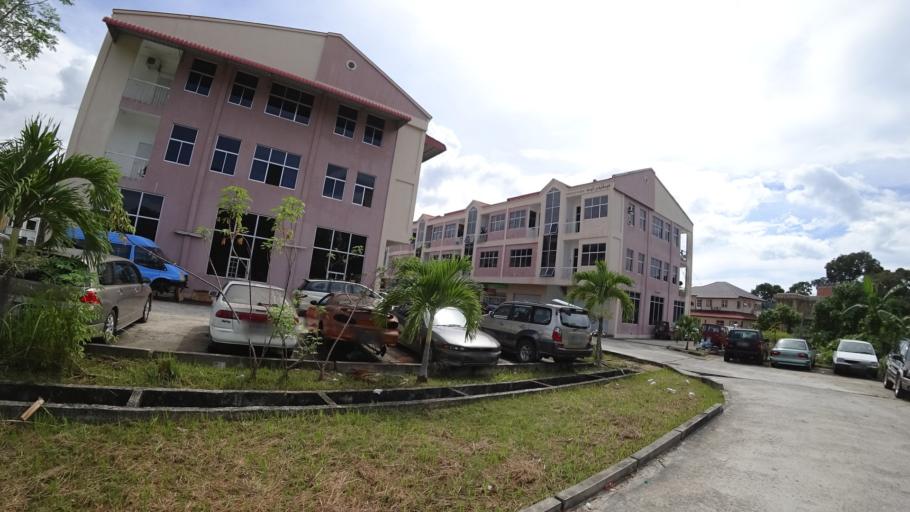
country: BN
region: Brunei and Muara
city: Bandar Seri Begawan
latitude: 4.8895
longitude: 114.8410
